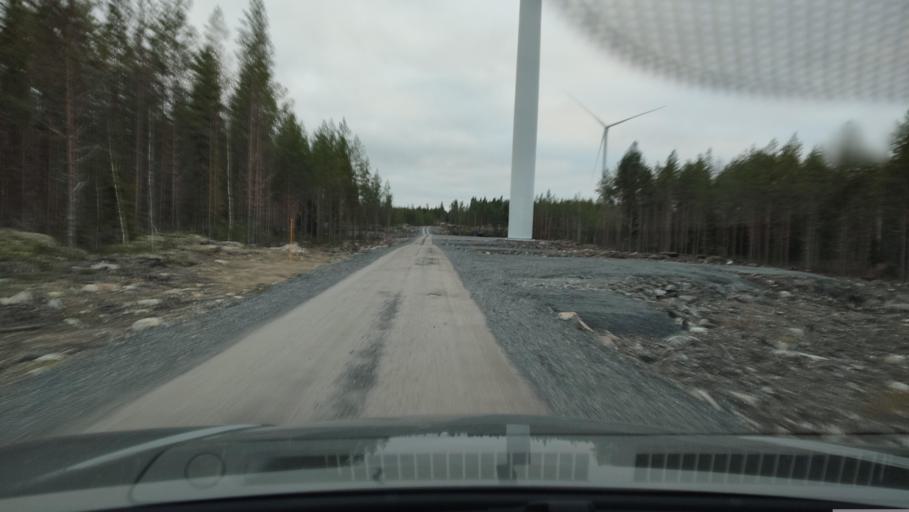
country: FI
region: Southern Ostrobothnia
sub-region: Suupohja
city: Karijoki
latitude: 62.1883
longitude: 21.5733
